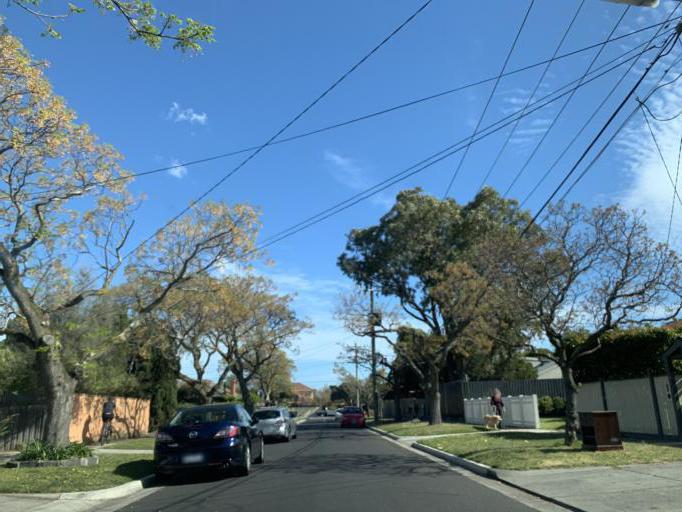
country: AU
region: Victoria
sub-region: Bayside
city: Hampton East
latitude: -37.9527
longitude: 145.0191
